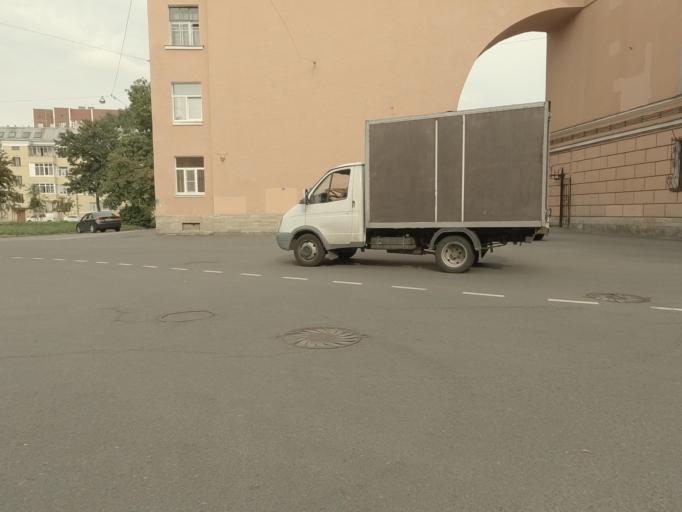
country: RU
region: St.-Petersburg
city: Admiralteisky
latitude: 59.8991
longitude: 30.2817
